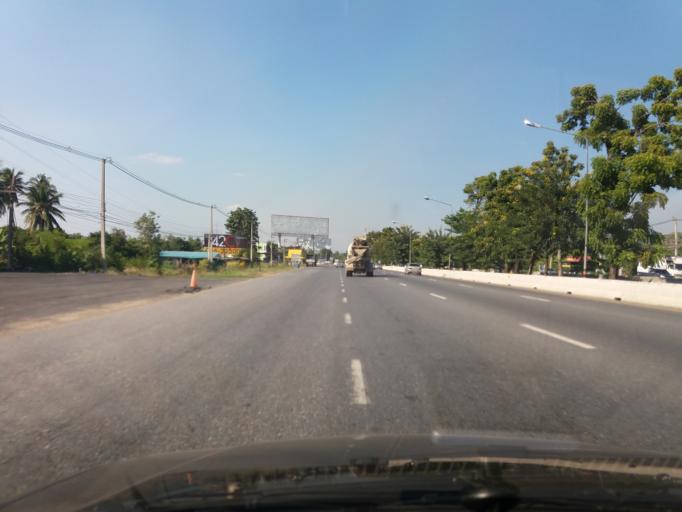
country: TH
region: Nakhon Sawan
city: Krok Phra
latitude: 15.6109
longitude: 100.1213
